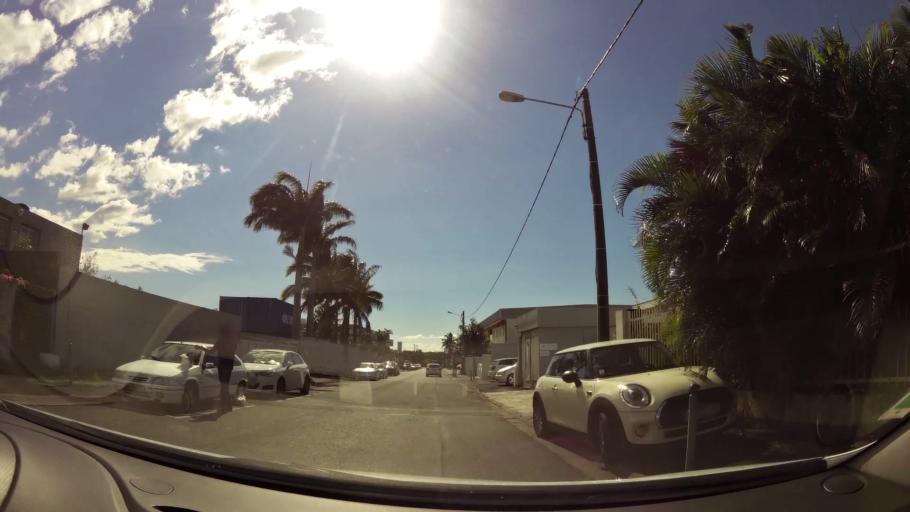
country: RE
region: Reunion
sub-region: Reunion
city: Saint-Denis
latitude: -20.8907
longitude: 55.4965
